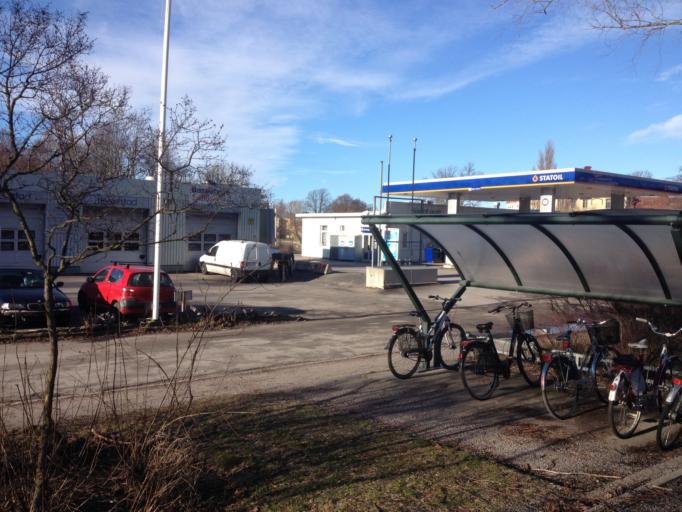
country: SE
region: Vaestra Goetaland
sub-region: Mariestads Kommun
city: Mariestad
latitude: 58.7053
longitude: 13.8212
